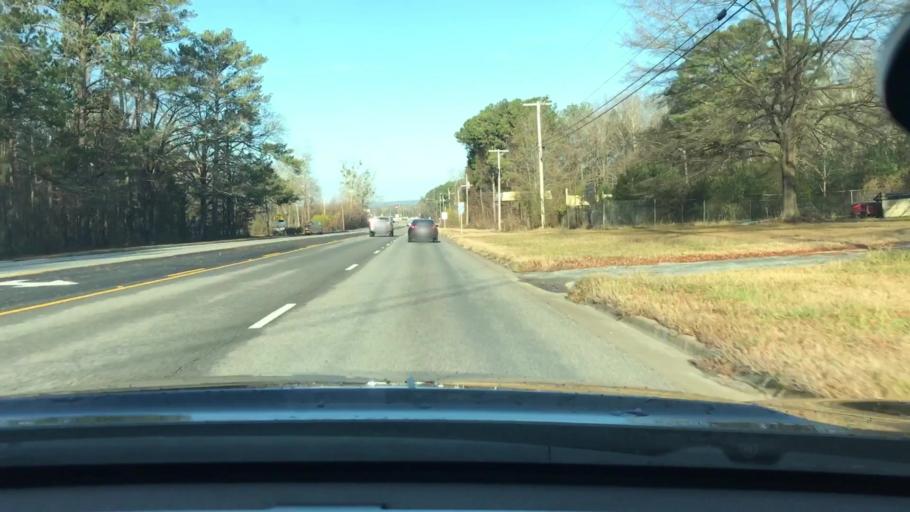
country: US
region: Alabama
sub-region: Shelby County
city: Harpersville
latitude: 33.3401
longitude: -86.4309
